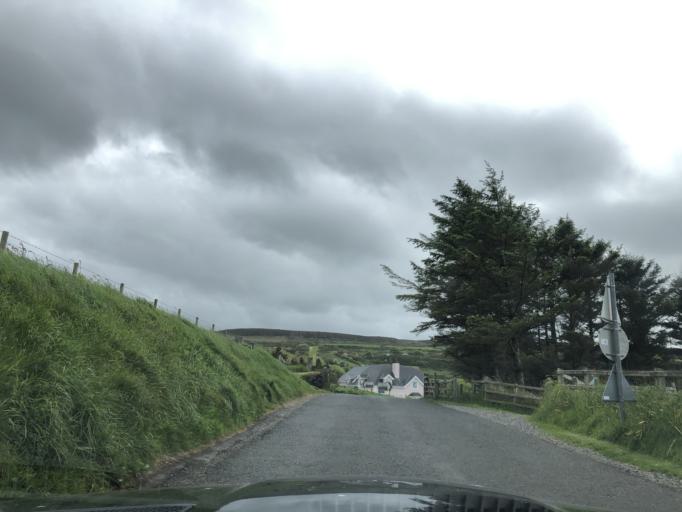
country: GB
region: Northern Ireland
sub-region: Moyle District
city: Ballycastle
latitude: 55.2377
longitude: -6.3506
